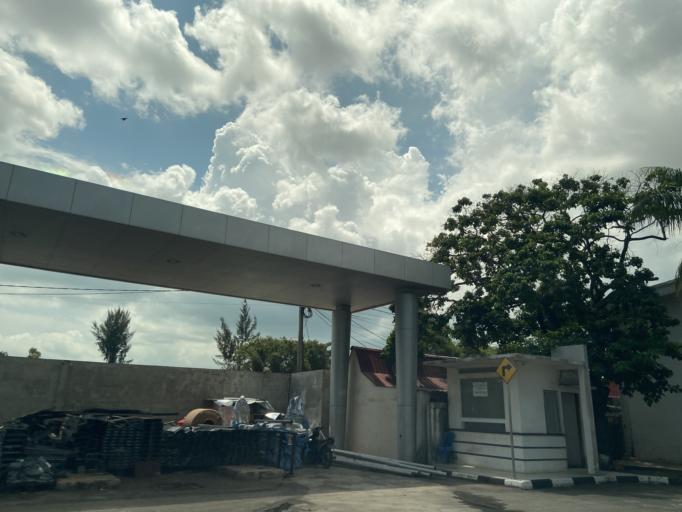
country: SG
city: Singapore
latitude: 1.1562
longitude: 103.9989
